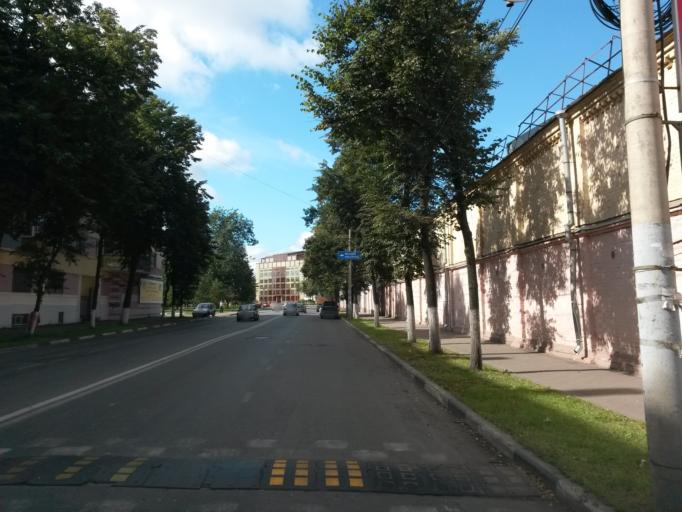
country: RU
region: Jaroslavl
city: Yaroslavl
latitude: 57.6357
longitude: 39.8754
